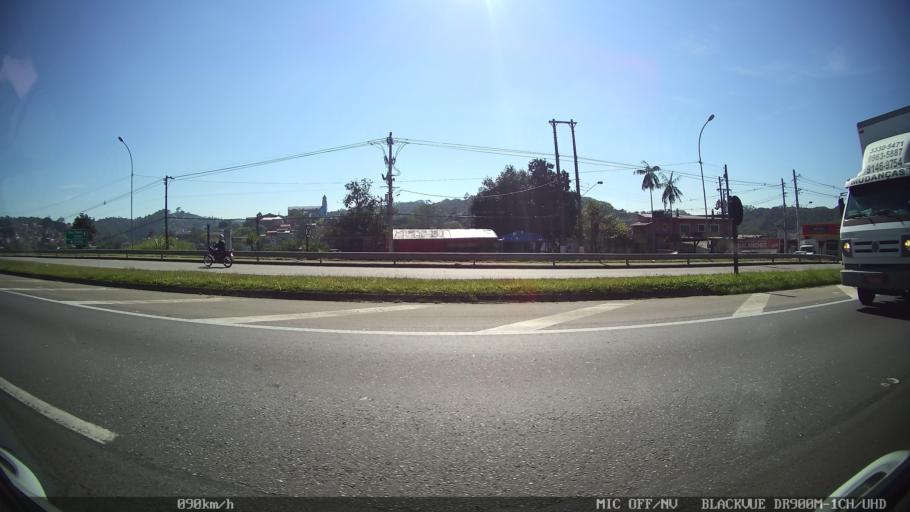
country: BR
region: Sao Paulo
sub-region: Juquitiba
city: Juquitiba
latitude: -23.9364
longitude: -47.0670
